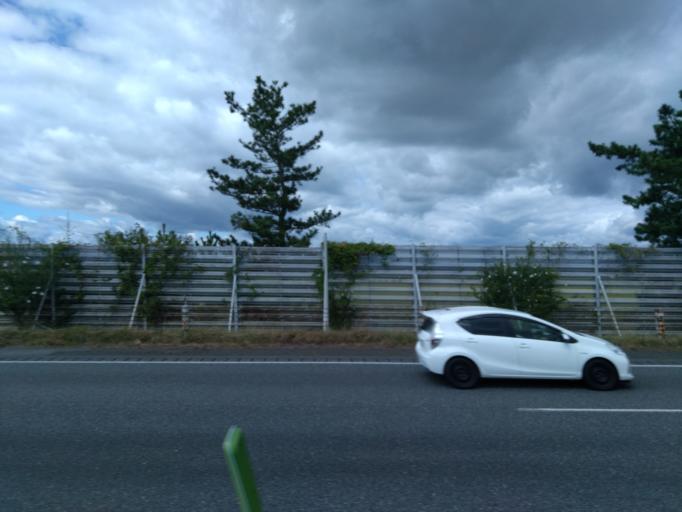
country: JP
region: Miyagi
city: Furukawa
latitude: 38.5866
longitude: 140.9303
